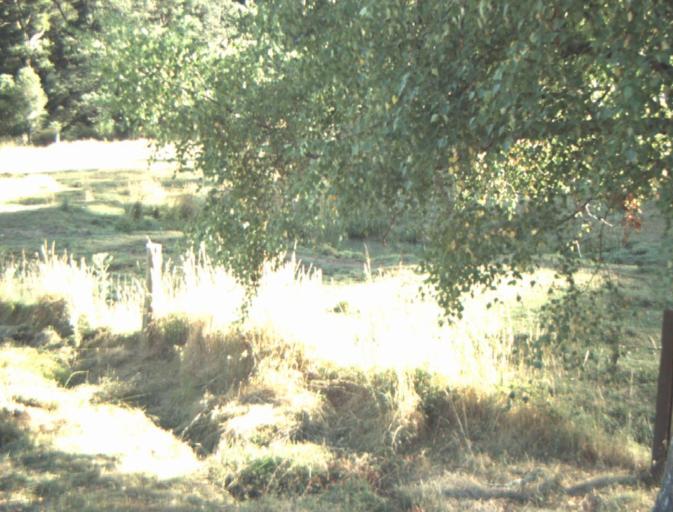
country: AU
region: Tasmania
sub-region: Launceston
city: Mayfield
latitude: -41.2877
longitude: 147.1973
